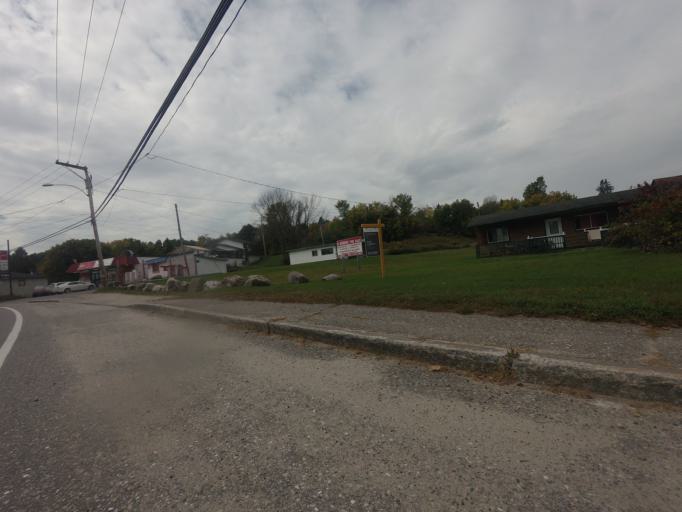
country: CA
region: Quebec
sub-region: Outaouais
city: Wakefield
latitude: 45.9531
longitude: -75.9455
